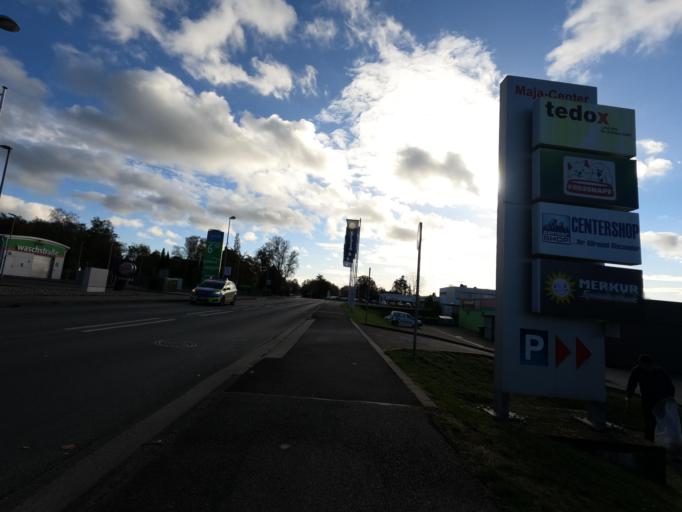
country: DE
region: North Rhine-Westphalia
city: Huckelhoven
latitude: 51.0520
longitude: 6.2182
